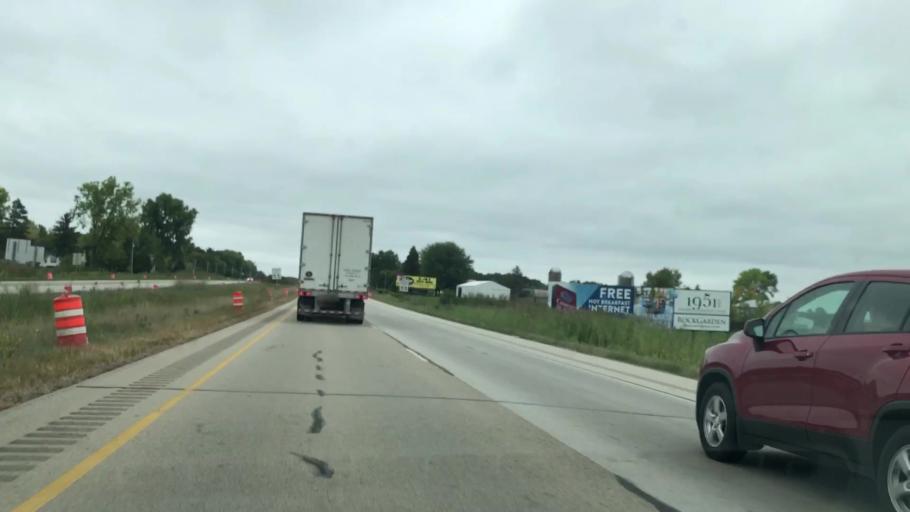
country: US
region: Wisconsin
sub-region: Brown County
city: Suamico
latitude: 44.6593
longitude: -88.0503
